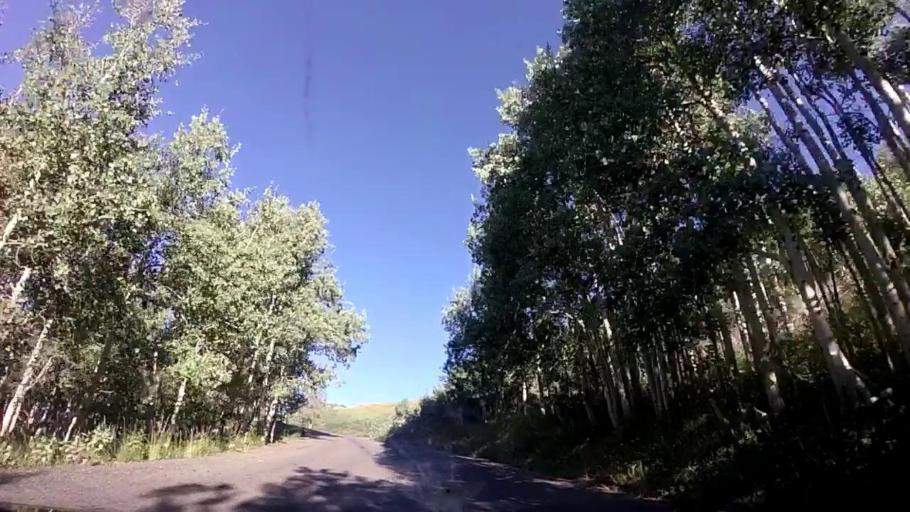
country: US
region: Utah
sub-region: Summit County
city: Park City
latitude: 40.6086
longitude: -111.5285
